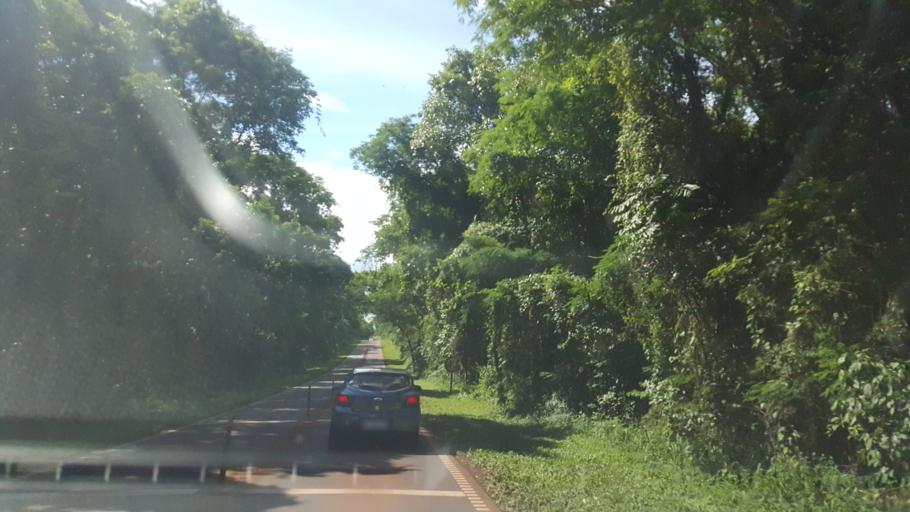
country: AR
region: Misiones
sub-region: Departamento de Iguazu
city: Puerto Iguazu
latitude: -25.6856
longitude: -54.4823
